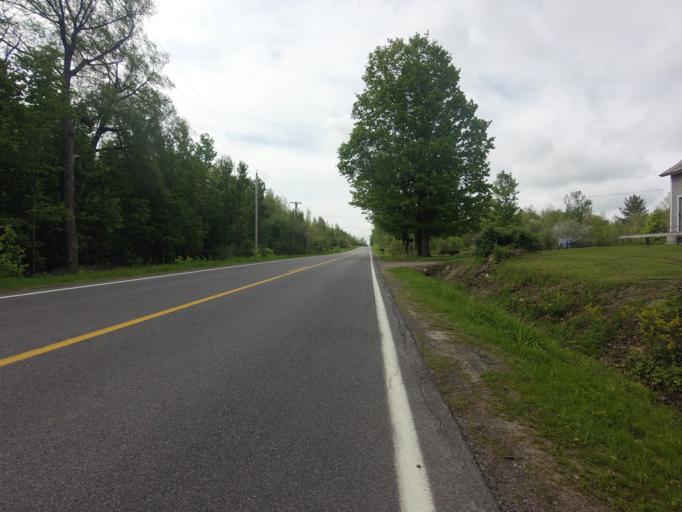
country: CA
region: Ontario
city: Cornwall
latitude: 44.7430
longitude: -74.6668
